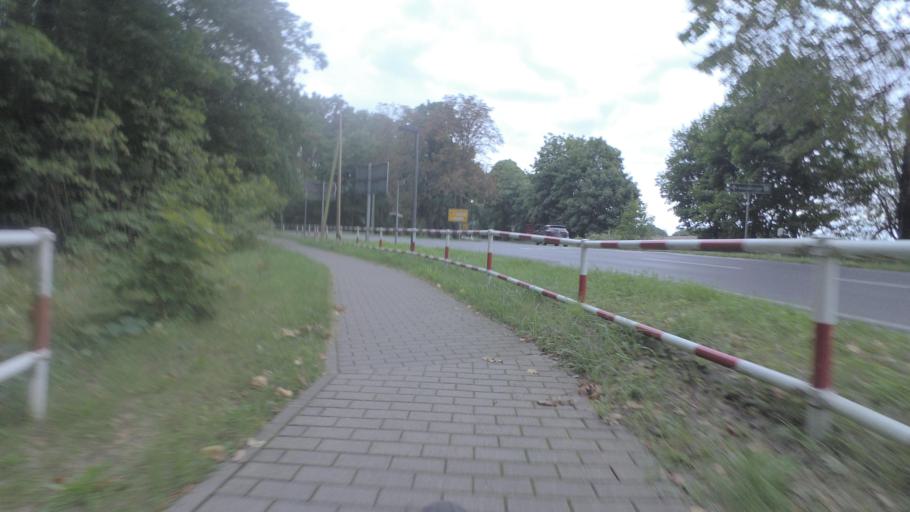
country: DE
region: Brandenburg
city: Hoppegarten
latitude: 52.4980
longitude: 13.6452
